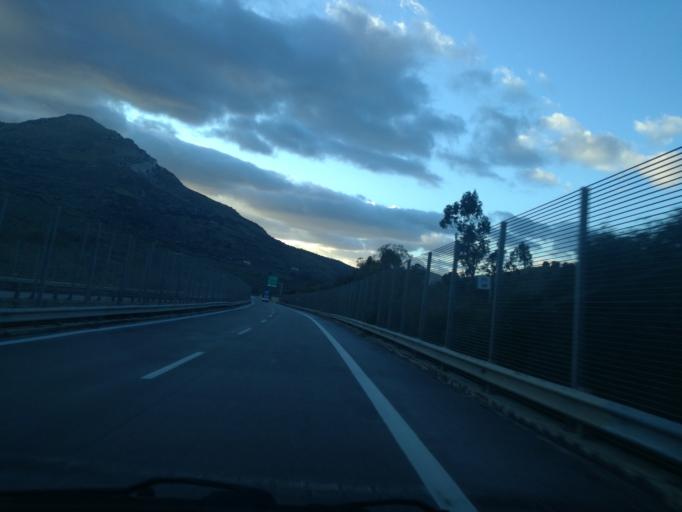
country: IT
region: Sicily
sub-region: Palermo
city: Scillato
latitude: 37.8359
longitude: 13.9376
